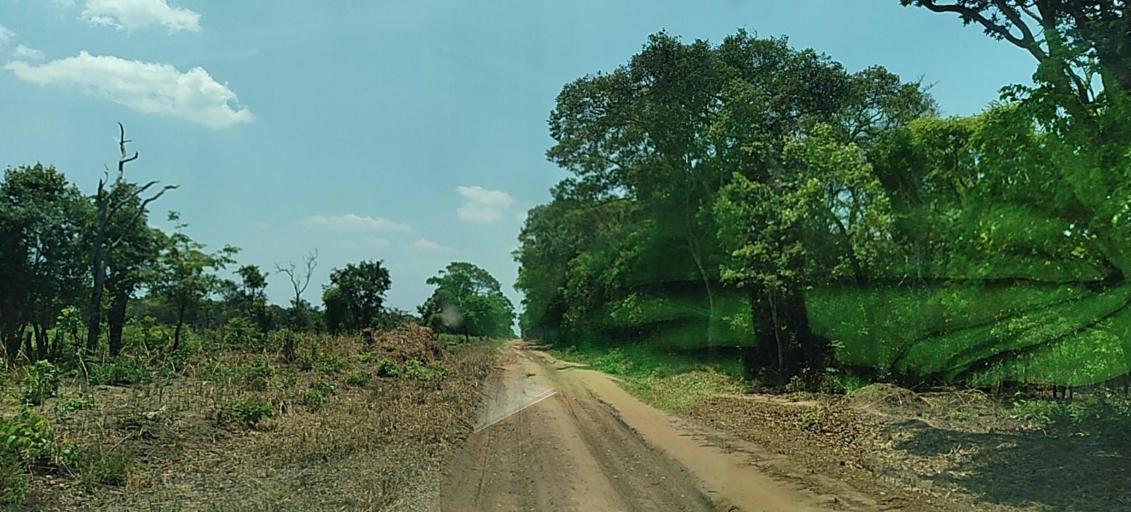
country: CD
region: Katanga
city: Kolwezi
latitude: -11.3902
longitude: 25.2216
